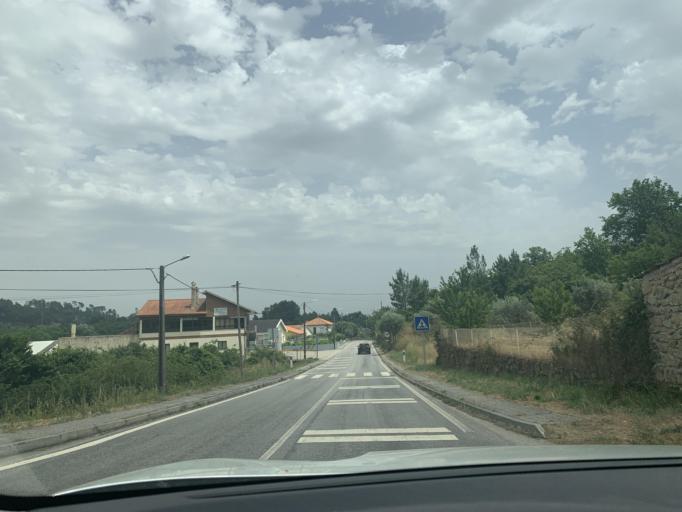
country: PT
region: Viseu
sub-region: Mangualde
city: Mangualde
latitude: 40.5644
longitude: -7.7202
